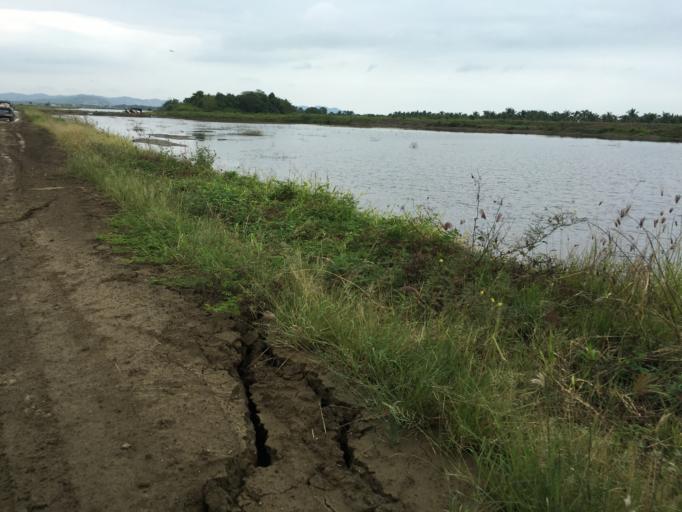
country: EC
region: Manabi
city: Pedernales
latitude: -0.1504
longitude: -80.2445
